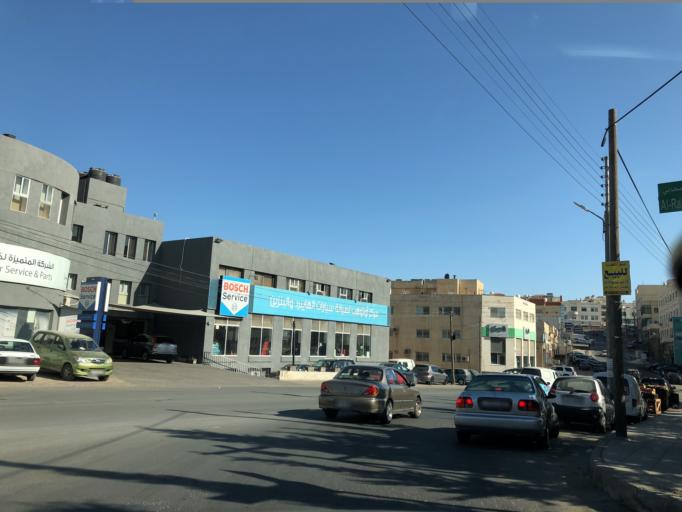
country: JO
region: Amman
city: Wadi as Sir
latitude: 31.9437
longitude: 35.8467
